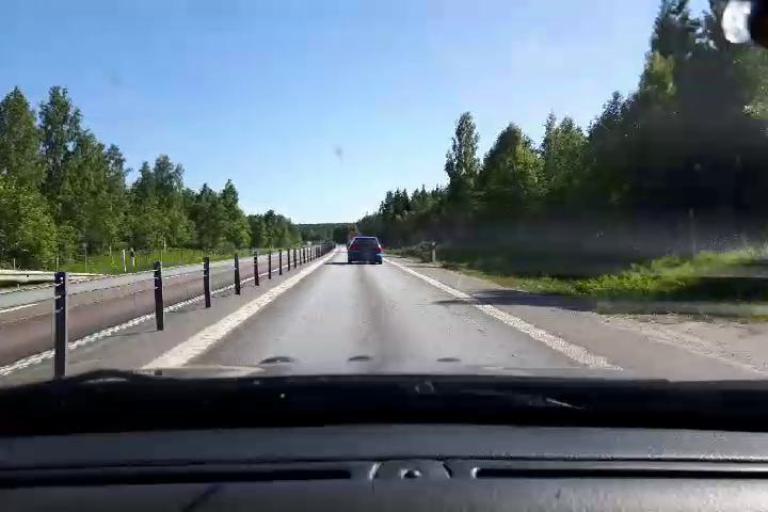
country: SE
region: Gaevleborg
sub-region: Gavle Kommun
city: Norrsundet
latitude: 60.9100
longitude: 17.0143
